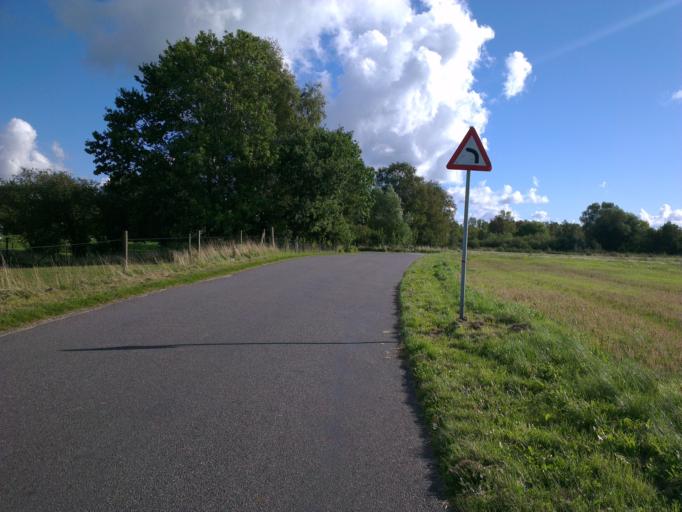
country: DK
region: Capital Region
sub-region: Frederikssund Kommune
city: Frederikssund
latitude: 55.7866
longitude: 12.0306
